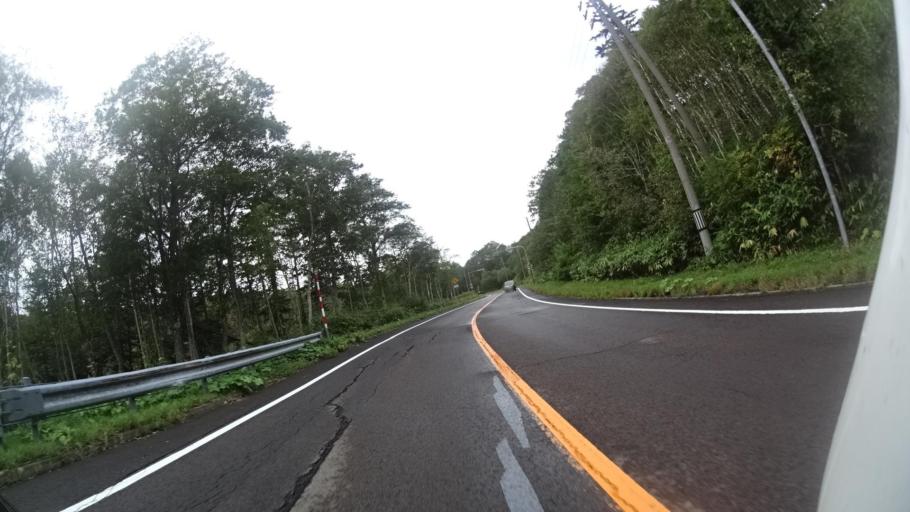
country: JP
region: Hokkaido
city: Shibetsu
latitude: 43.7660
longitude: 144.7939
